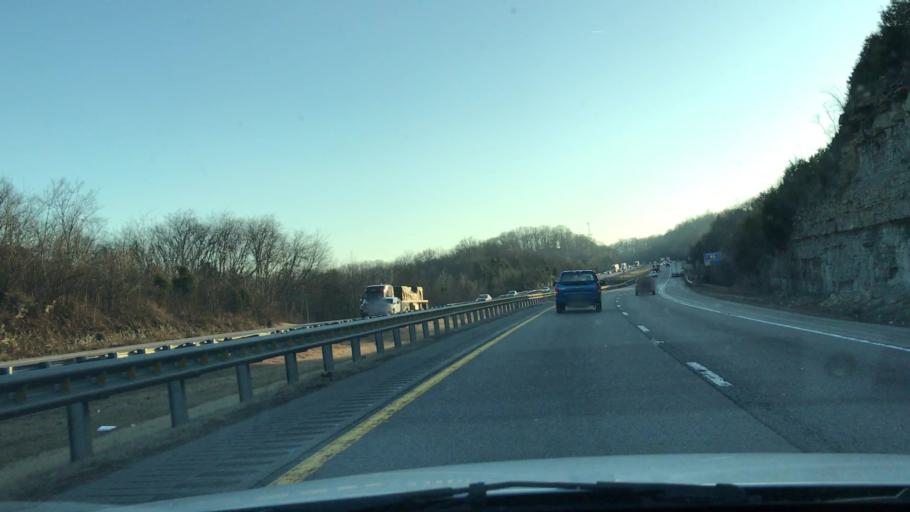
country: US
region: Tennessee
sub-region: Sumner County
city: Millersville
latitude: 36.3684
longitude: -86.7131
